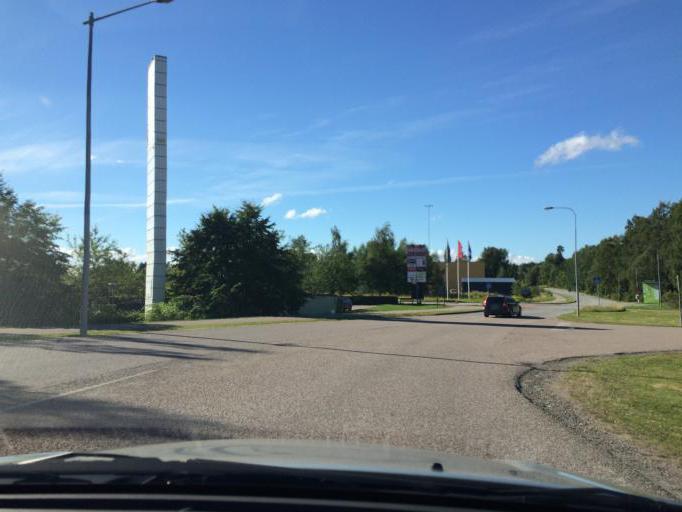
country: SE
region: Vaestmanland
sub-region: Vasteras
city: Hokasen
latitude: 59.6079
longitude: 16.6312
